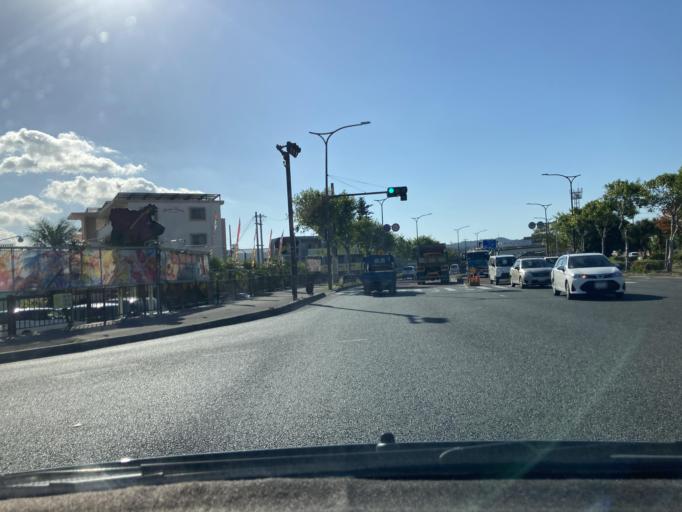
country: JP
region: Okinawa
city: Ishikawa
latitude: 26.4334
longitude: 127.8336
